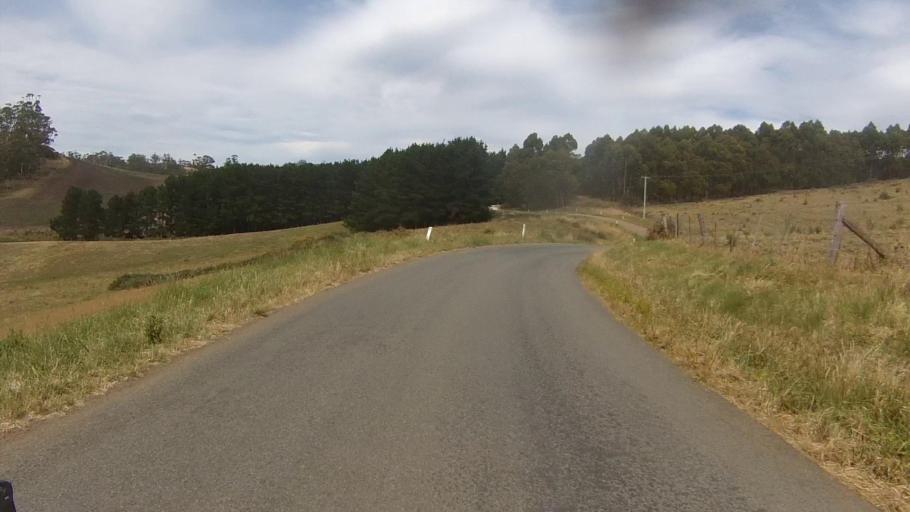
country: AU
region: Tasmania
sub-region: Sorell
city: Sorell
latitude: -42.8097
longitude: 147.8316
